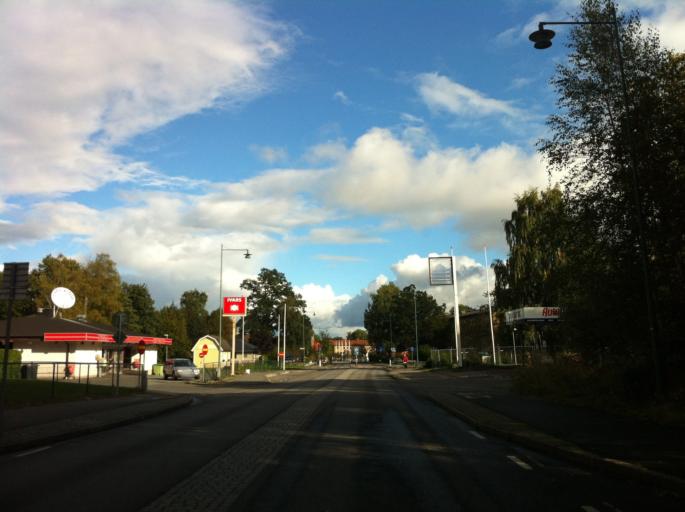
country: SE
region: Skane
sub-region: Hassleholms Kommun
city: Tormestorp
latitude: 56.1620
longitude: 13.5998
